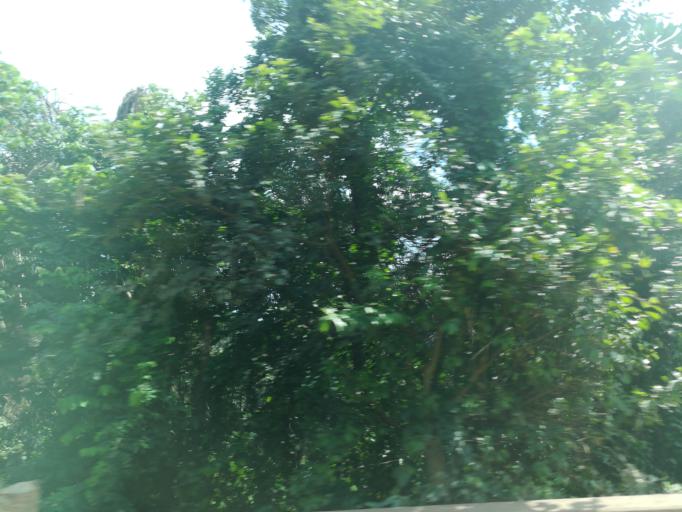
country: NG
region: Lagos
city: Ikorodu
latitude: 6.6565
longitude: 3.6891
